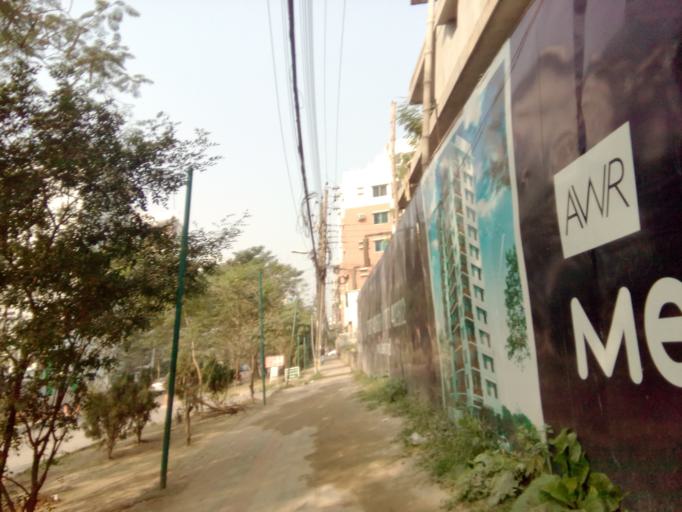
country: BD
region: Dhaka
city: Tungi
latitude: 23.8176
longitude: 90.4300
